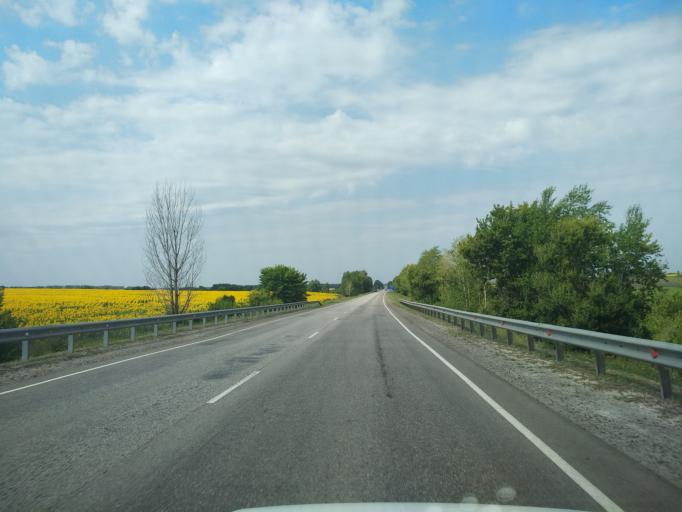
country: RU
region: Voronezj
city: Verkhnyaya Khava
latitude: 51.6922
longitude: 39.9422
